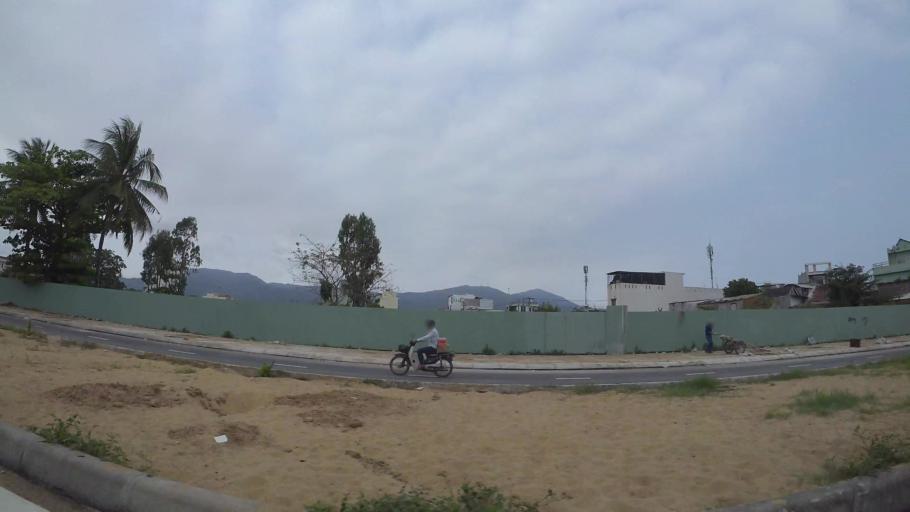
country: VN
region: Da Nang
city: Son Tra
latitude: 16.0830
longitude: 108.2388
